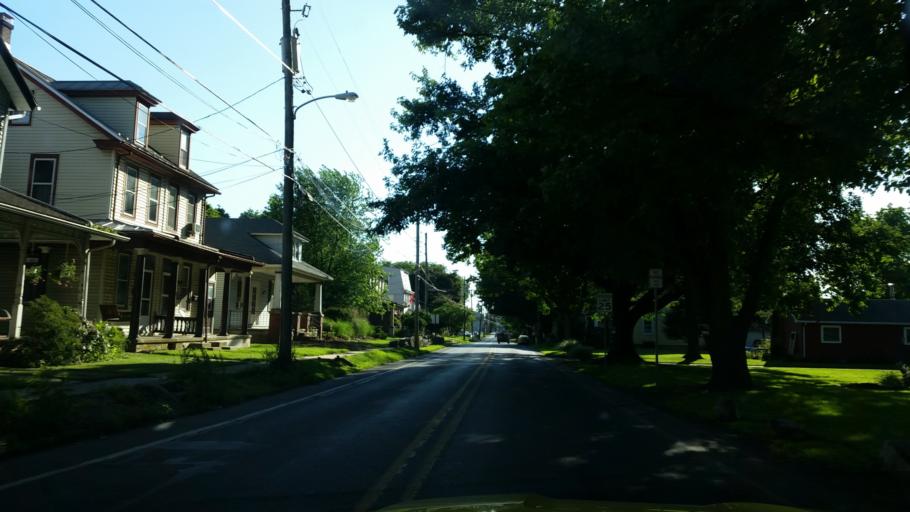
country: US
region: Pennsylvania
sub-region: Lebanon County
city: Avon
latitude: 40.3464
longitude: -76.3849
